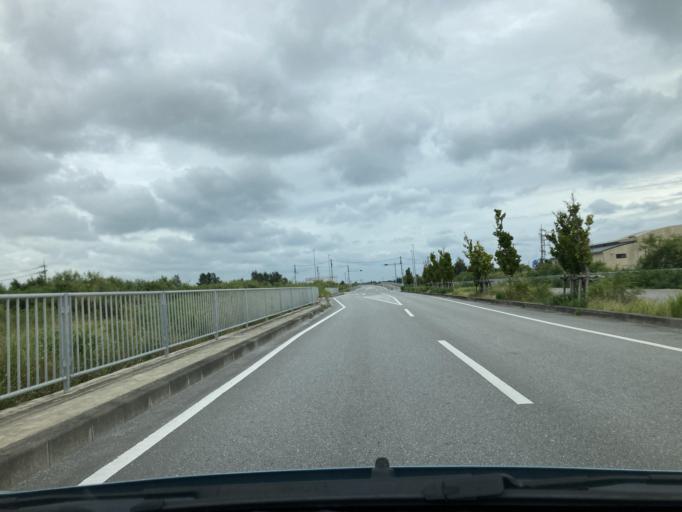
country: JP
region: Okinawa
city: Ginowan
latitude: 26.2125
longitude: 127.7677
